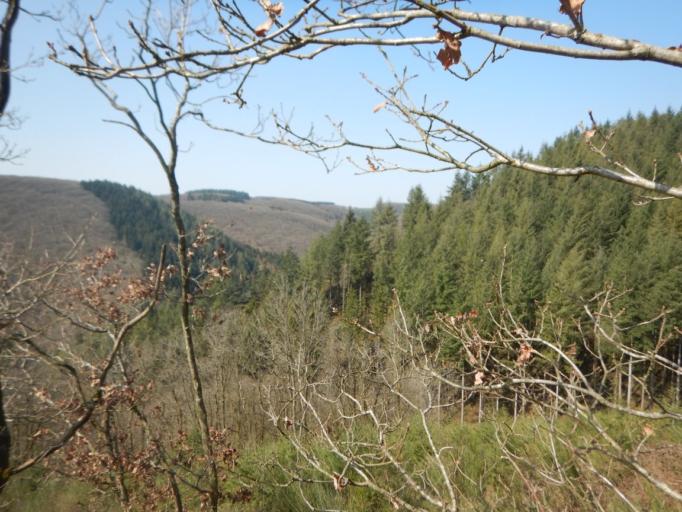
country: LU
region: Diekirch
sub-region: Canton de Diekirch
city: Bourscheid
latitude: 49.9492
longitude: 6.0699
